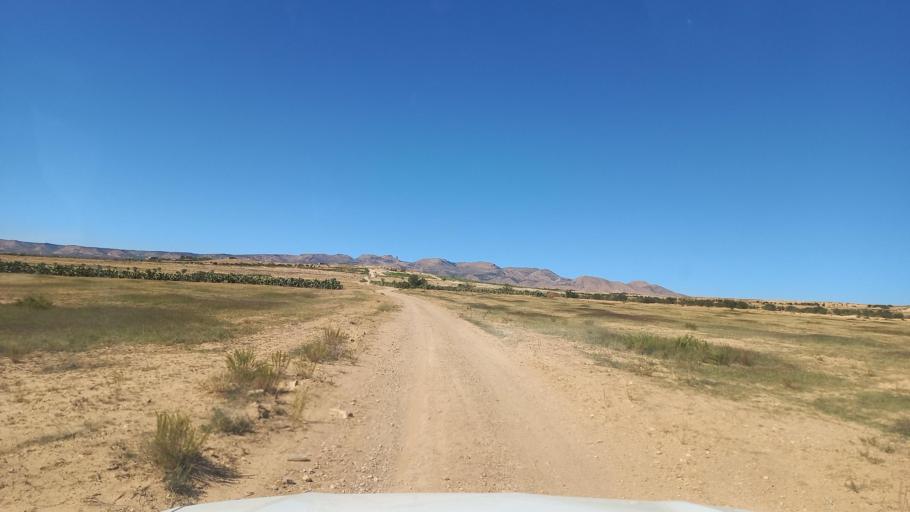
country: TN
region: Al Qasrayn
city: Sbiba
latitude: 35.3703
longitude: 9.0842
